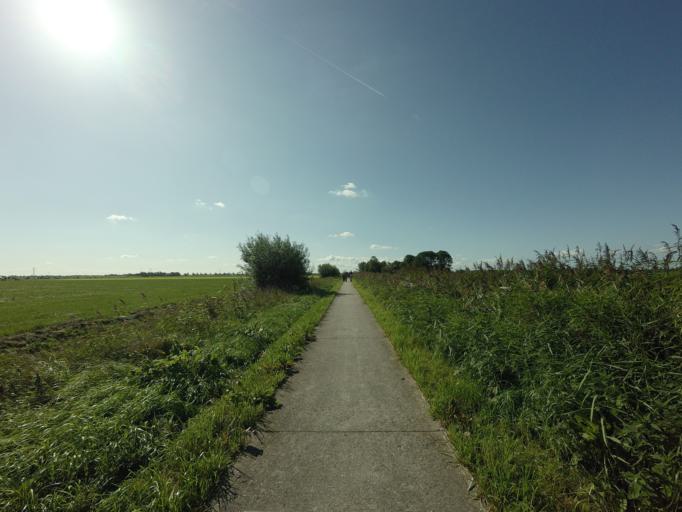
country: NL
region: Friesland
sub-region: Gemeente Boarnsterhim
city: Reduzum
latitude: 53.1304
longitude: 5.7561
